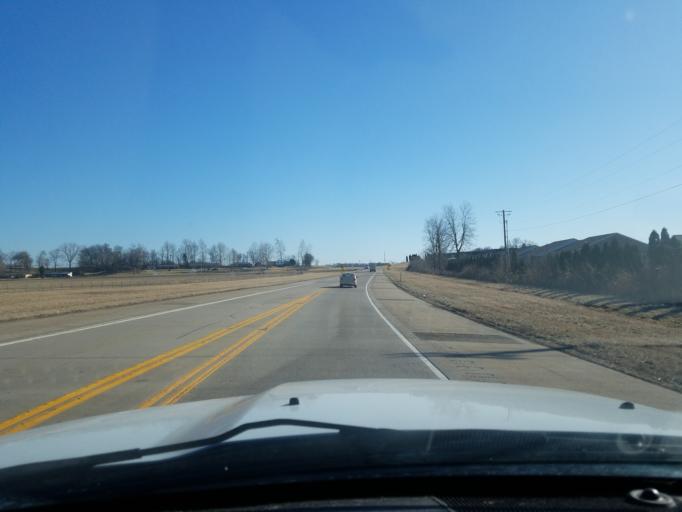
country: US
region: Kentucky
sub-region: Henderson County
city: Henderson
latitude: 37.7979
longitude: -87.6458
